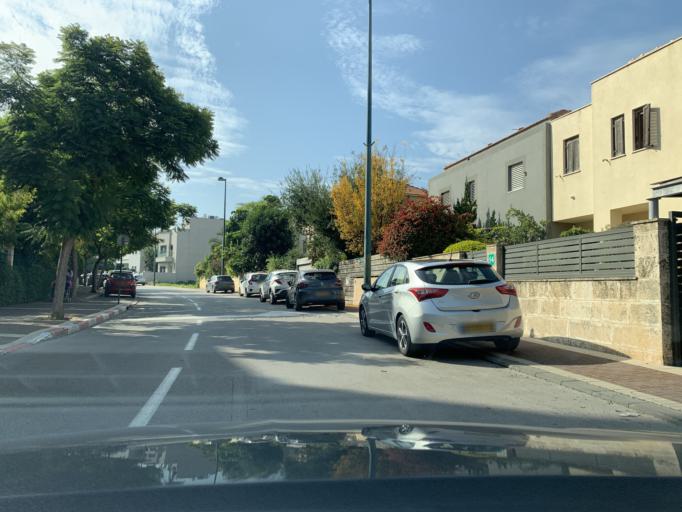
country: IL
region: Central District
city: Ganne Tiqwa
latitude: 32.0587
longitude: 34.8561
